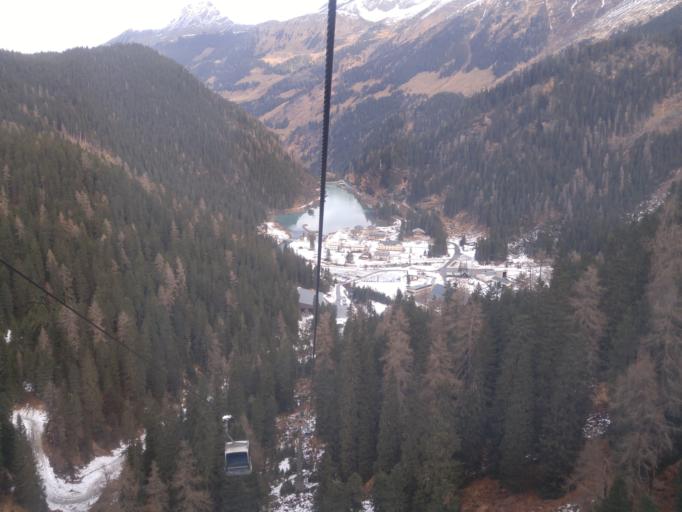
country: AT
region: Salzburg
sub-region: Politischer Bezirk Zell am See
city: Niedernsill
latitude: 47.1640
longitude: 12.6240
